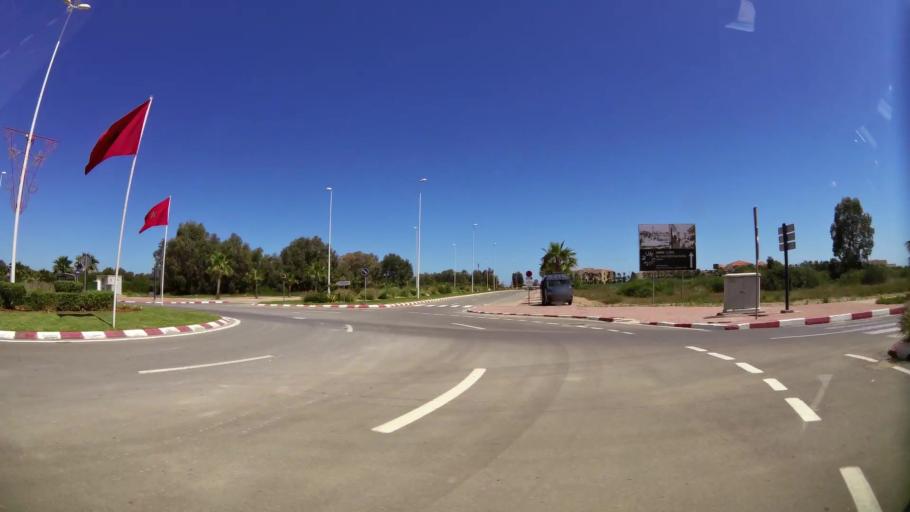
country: MA
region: Oriental
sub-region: Berkane-Taourirt
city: Madagh
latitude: 35.0971
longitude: -2.2773
